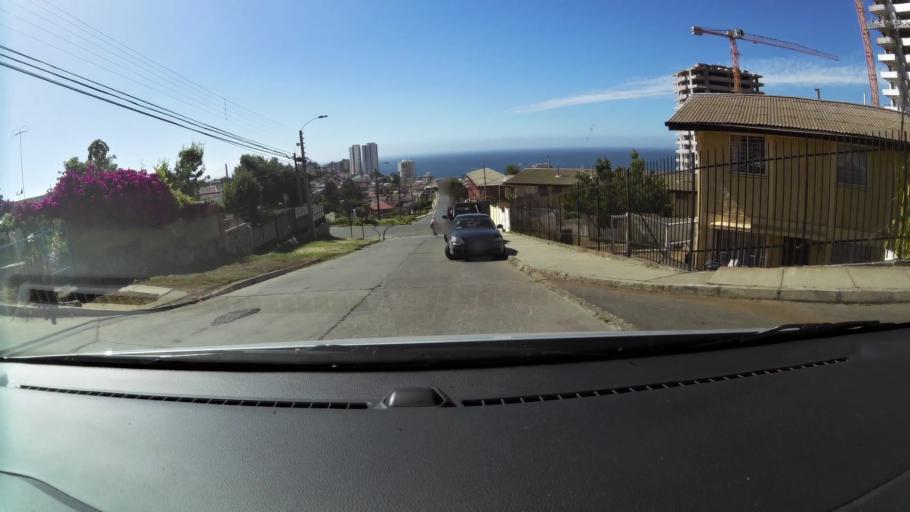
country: CL
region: Valparaiso
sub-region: Provincia de Valparaiso
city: Vina del Mar
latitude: -33.0350
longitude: -71.5739
